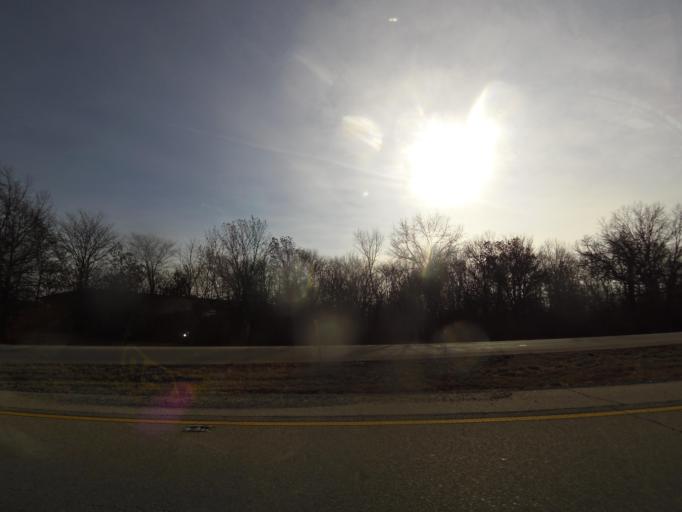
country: US
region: Illinois
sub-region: Macon County
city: Forsyth
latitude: 39.9069
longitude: -88.9534
